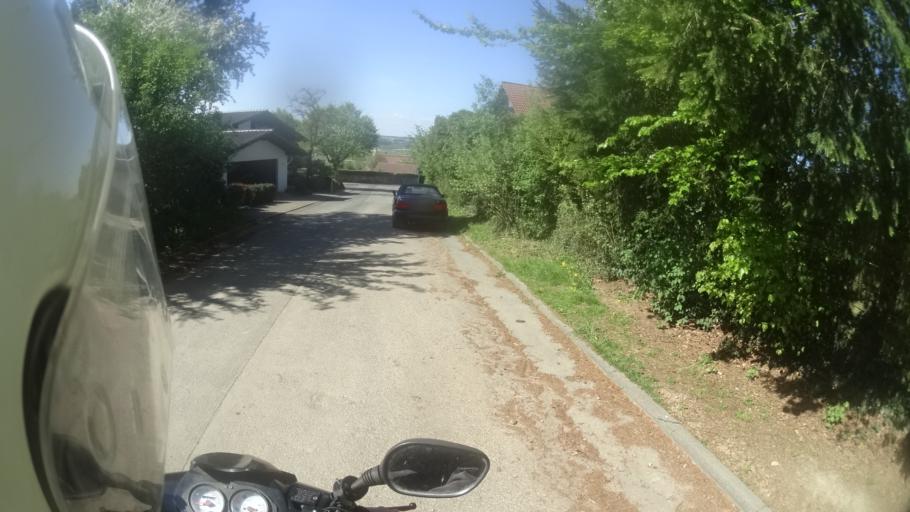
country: DE
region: Hesse
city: Taunusstein
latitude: 50.1284
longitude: 8.1442
